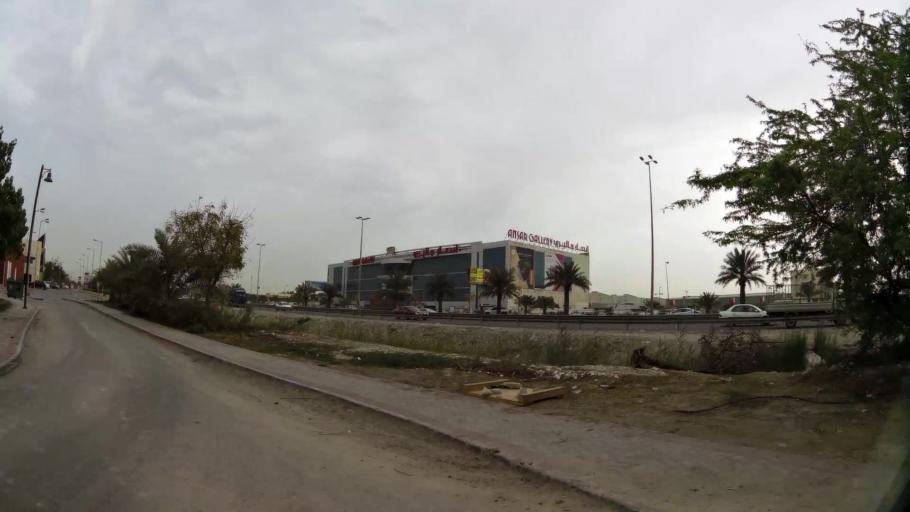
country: BH
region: Manama
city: Jidd Hafs
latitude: 26.1970
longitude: 50.5436
